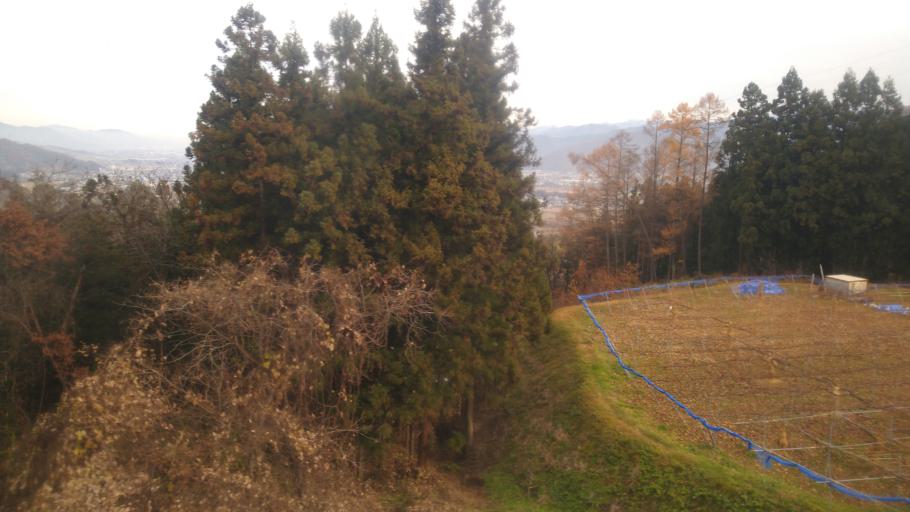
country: JP
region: Nagano
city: Nagano-shi
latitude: 36.5094
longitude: 138.0819
